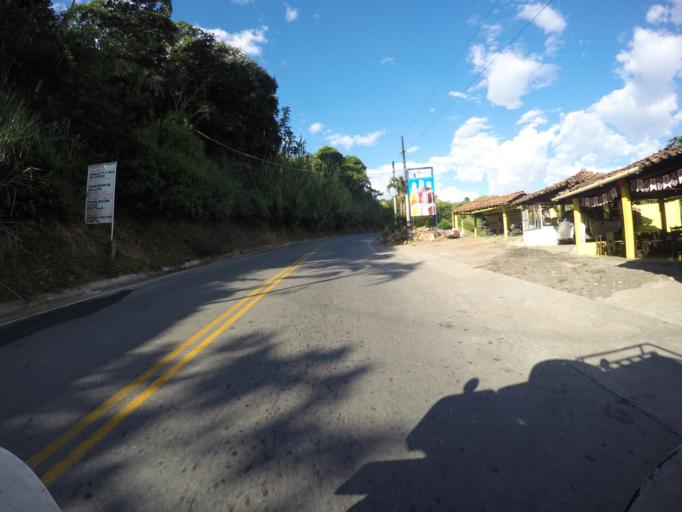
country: CO
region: Valle del Cauca
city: Alcala
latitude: 4.7055
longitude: -75.8431
